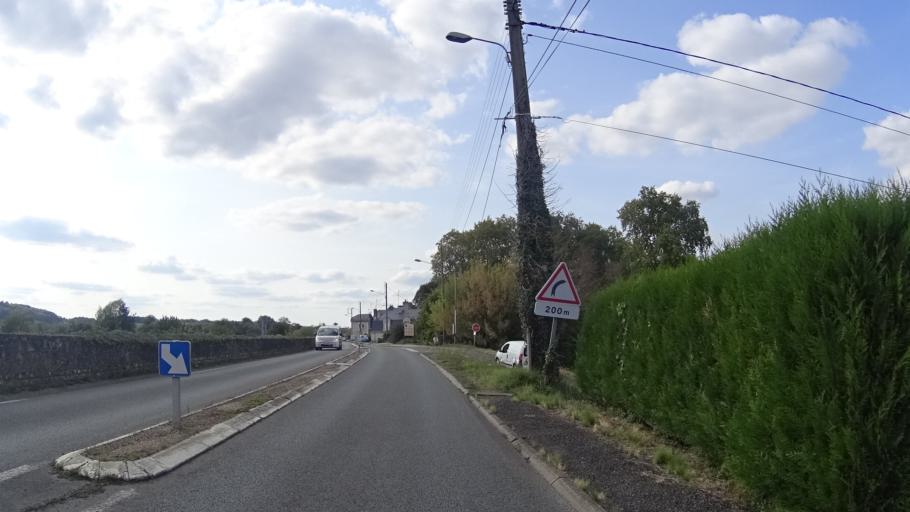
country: FR
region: Pays de la Loire
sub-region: Departement de Maine-et-Loire
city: Les Rosiers-sur-Loire
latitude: 47.3476
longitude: -0.2205
